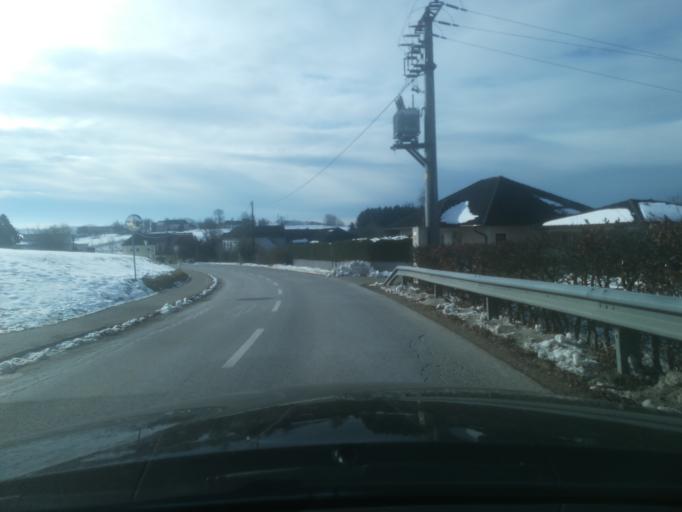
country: AT
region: Upper Austria
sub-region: Politischer Bezirk Perg
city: Perg
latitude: 48.3216
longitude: 14.6245
